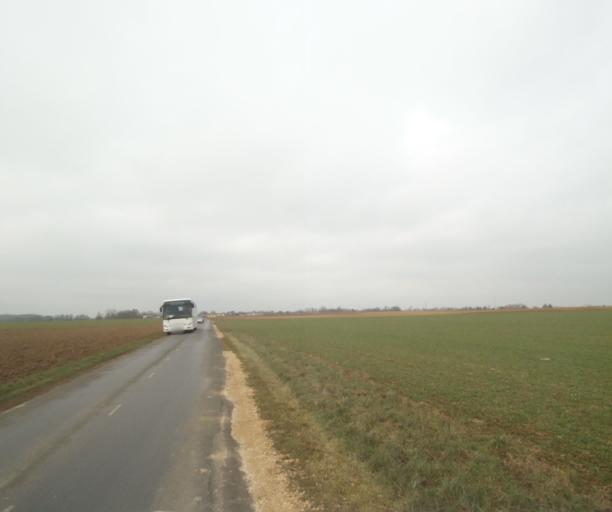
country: FR
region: Champagne-Ardenne
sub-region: Departement de la Marne
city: Pargny-sur-Saulx
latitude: 48.6882
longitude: 4.8151
